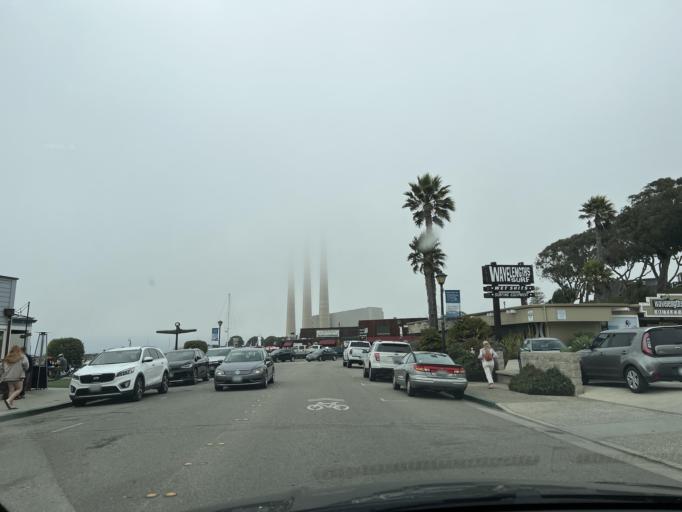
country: US
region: California
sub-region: San Luis Obispo County
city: Morro Bay
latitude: 35.3672
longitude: -120.8537
